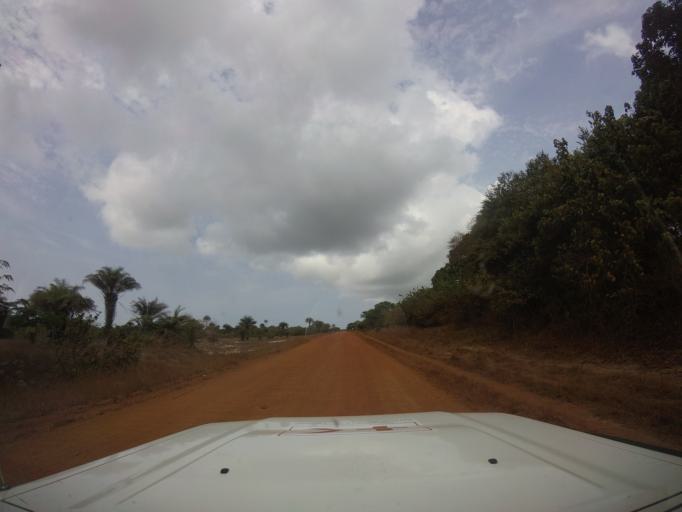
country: LR
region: Grand Cape Mount
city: Robertsport
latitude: 6.6913
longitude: -11.2644
